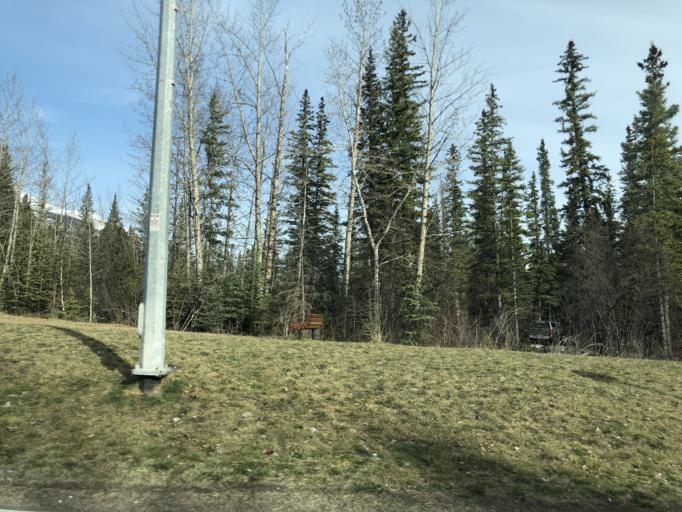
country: CA
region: Alberta
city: Canmore
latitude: 51.0856
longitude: -115.3665
